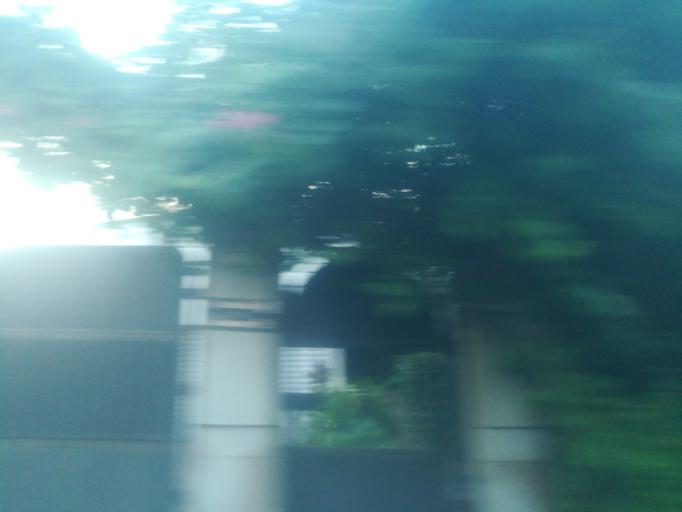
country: NG
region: Oyo
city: Ibadan
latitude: 7.4285
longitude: 3.9334
